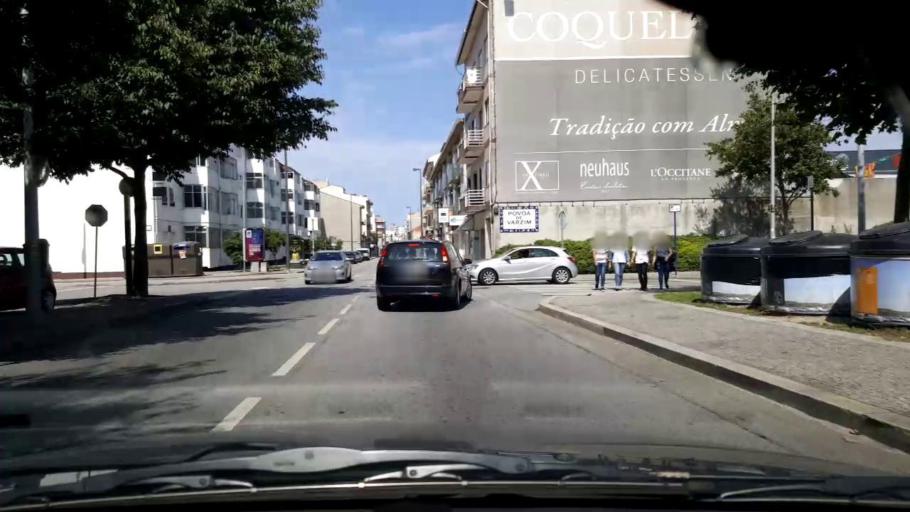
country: PT
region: Porto
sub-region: Povoa de Varzim
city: Povoa de Varzim
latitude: 41.3733
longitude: -8.7551
